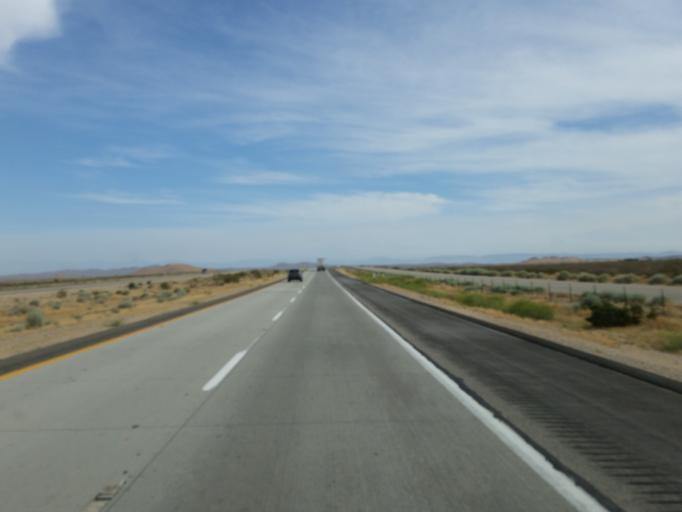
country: US
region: California
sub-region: Kern County
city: Mojave
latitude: 35.0553
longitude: -118.1133
